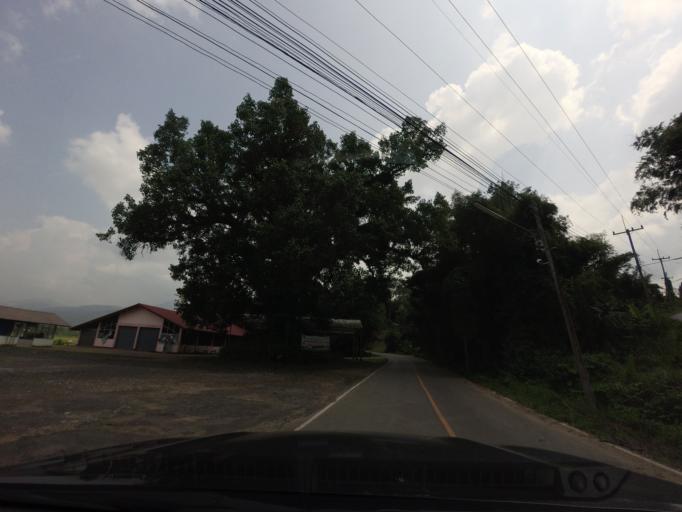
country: TH
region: Nan
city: Pua
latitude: 19.1703
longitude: 100.9273
